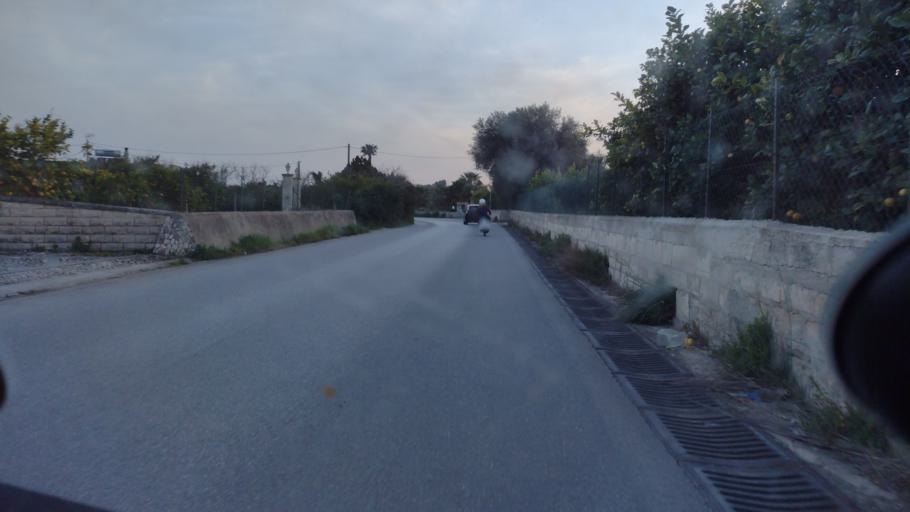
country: IT
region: Sicily
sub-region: Provincia di Siracusa
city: Avola
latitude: 36.8779
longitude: 15.1277
